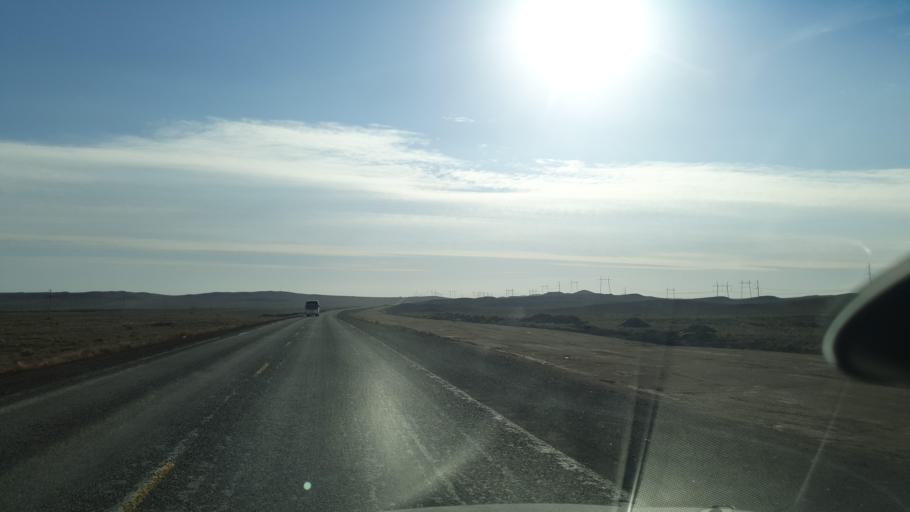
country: KZ
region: Zhambyl
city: Mynaral
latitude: 45.6865
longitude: 73.4008
